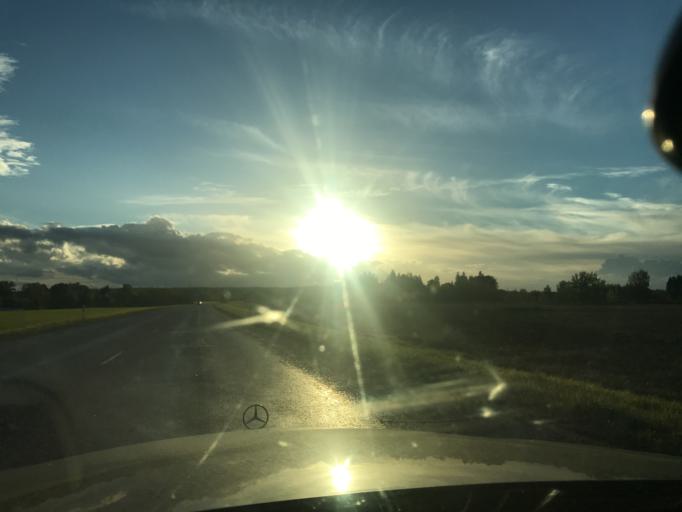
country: EE
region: Vorumaa
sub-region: Voru linn
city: Voru
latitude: 57.8639
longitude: 26.9172
